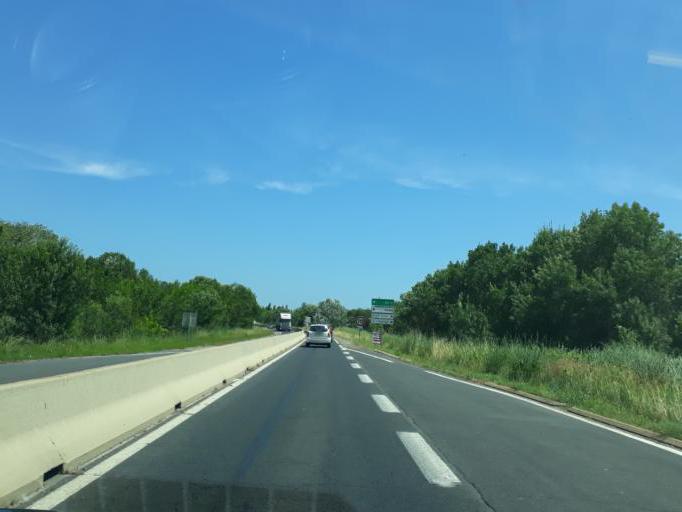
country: FR
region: Languedoc-Roussillon
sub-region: Departement de l'Herault
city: Vias
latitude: 43.3069
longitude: 3.4120
